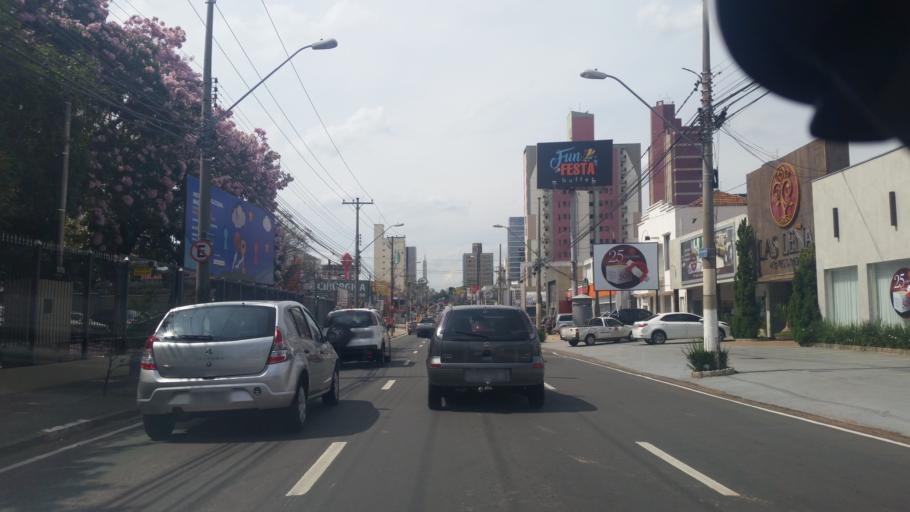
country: BR
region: Sao Paulo
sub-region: Campinas
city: Campinas
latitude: -22.8896
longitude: -47.0618
